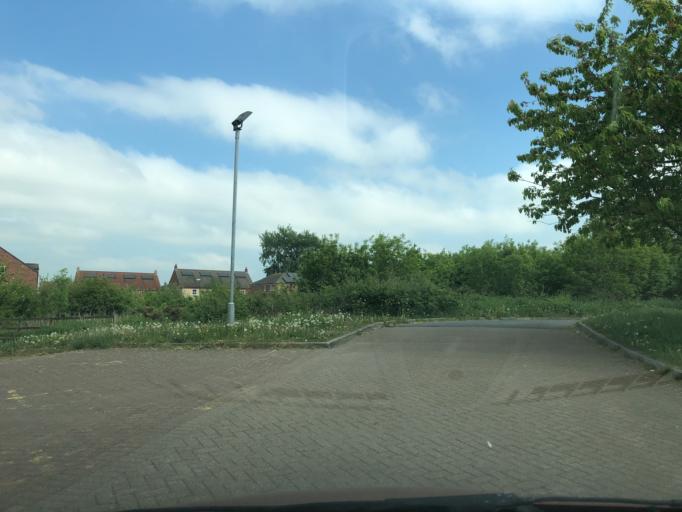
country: GB
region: England
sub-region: North Yorkshire
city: Catterick Garrison
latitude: 54.3810
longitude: -1.6816
